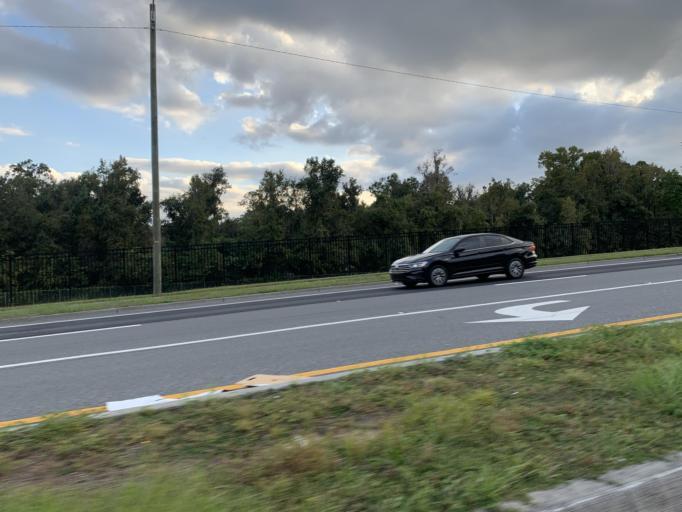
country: US
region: Florida
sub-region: Marion County
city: Ocala
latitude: 29.1562
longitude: -82.1320
